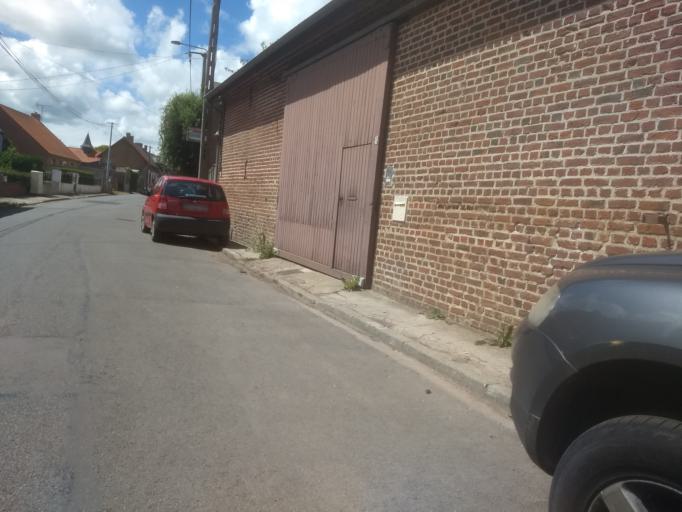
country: FR
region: Nord-Pas-de-Calais
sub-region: Departement du Pas-de-Calais
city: Riviere
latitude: 50.2454
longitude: 2.7192
